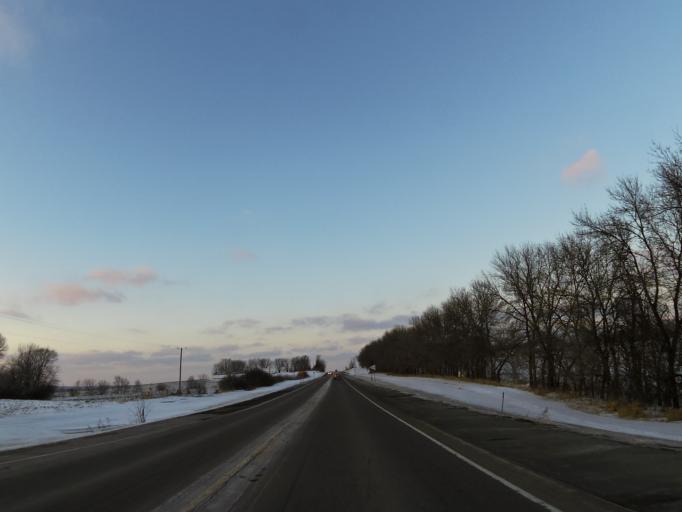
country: US
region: Minnesota
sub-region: Dakota County
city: Farmington
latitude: 44.6843
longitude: -93.1365
